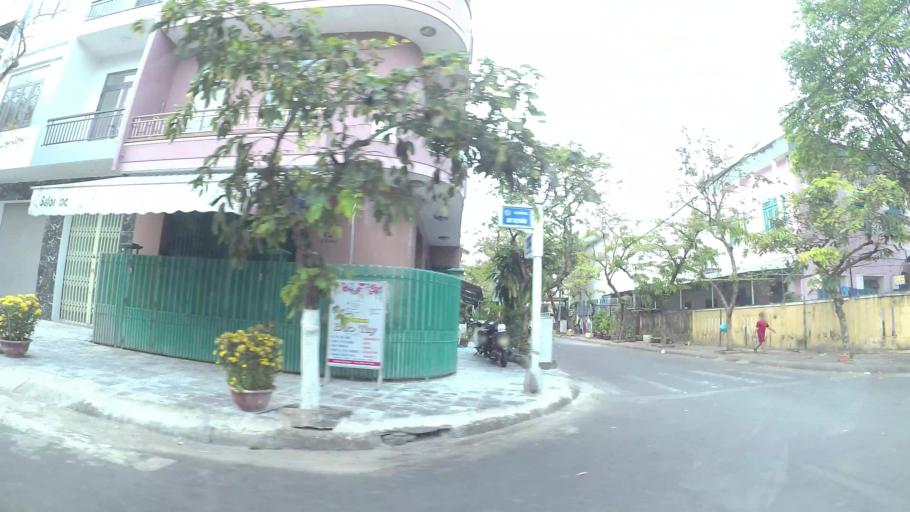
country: VN
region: Da Nang
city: Son Tra
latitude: 16.0526
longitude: 108.2345
